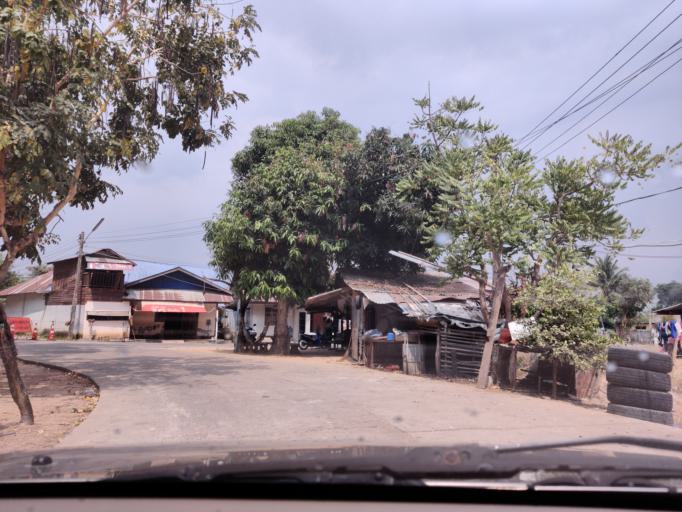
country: TH
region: Sisaket
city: Si Sa Ket
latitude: 15.1027
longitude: 104.3521
